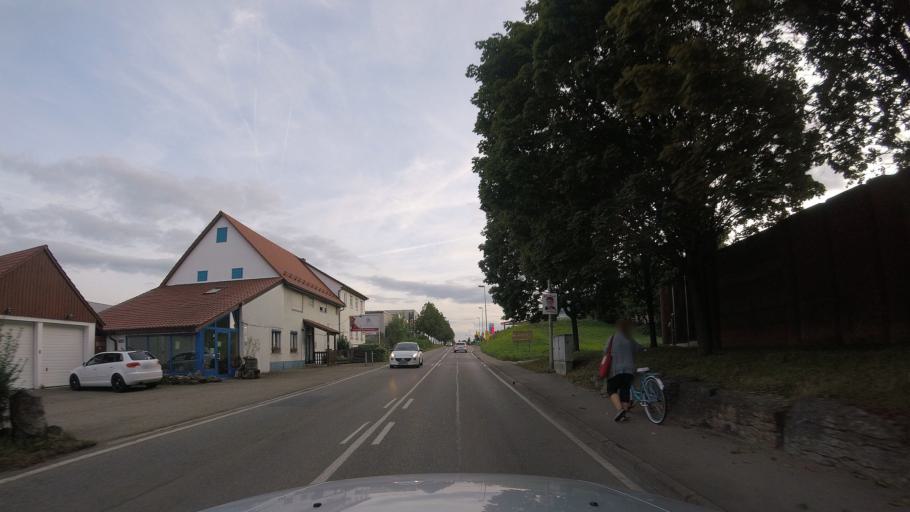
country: DE
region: Baden-Wuerttemberg
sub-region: Regierungsbezirk Stuttgart
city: Grossbottwar
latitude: 49.0053
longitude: 9.3002
